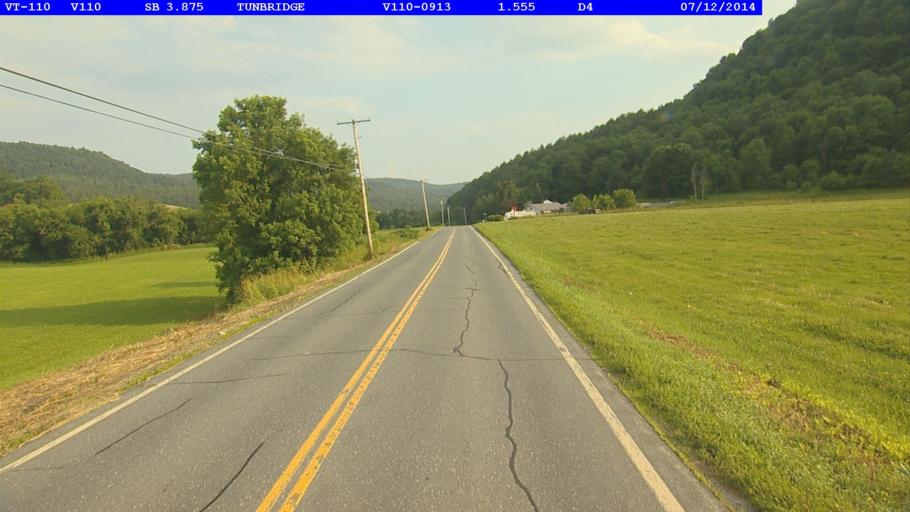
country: US
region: Vermont
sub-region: Orange County
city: Chelsea
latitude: 43.8732
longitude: -72.4988
